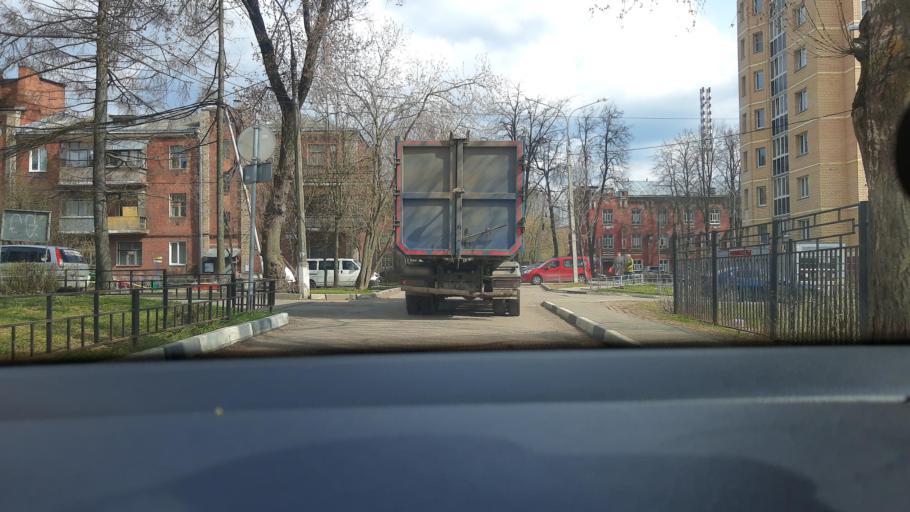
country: RU
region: Moskovskaya
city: Pirogovskiy
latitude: 55.9791
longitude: 37.7457
